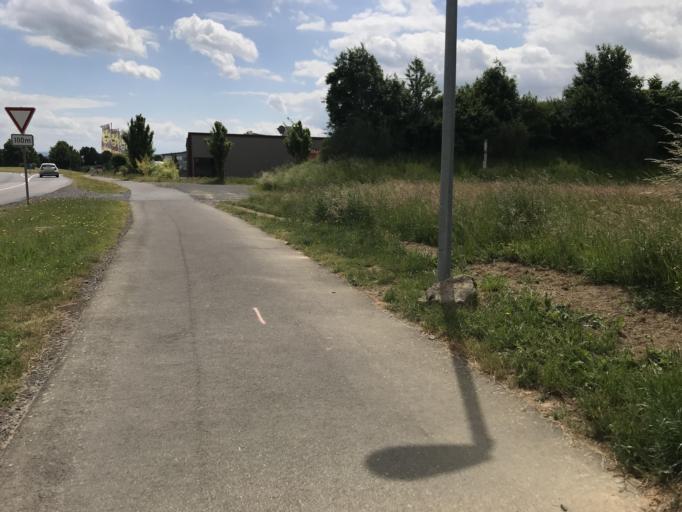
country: DE
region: Hesse
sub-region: Regierungsbezirk Kassel
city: Baunatal
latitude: 51.2692
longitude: 9.3767
